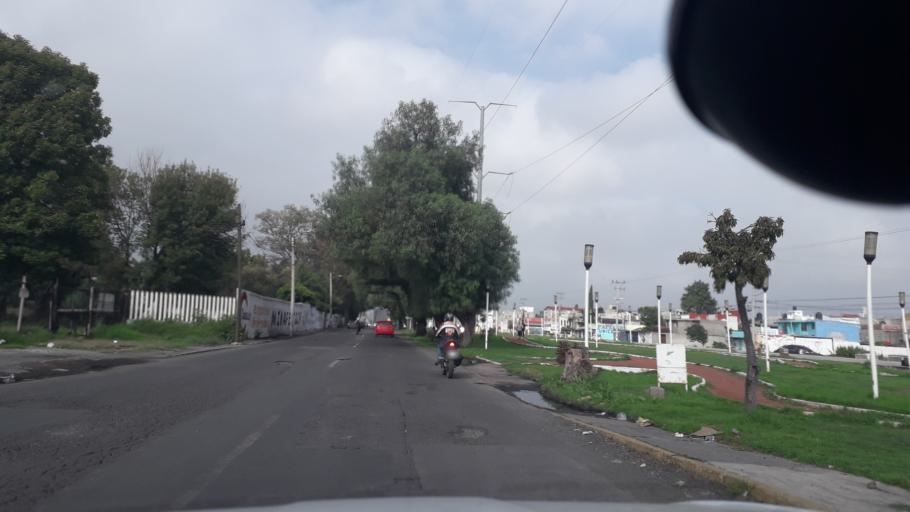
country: MX
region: Mexico
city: Coacalco
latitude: 19.6444
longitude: -99.0942
